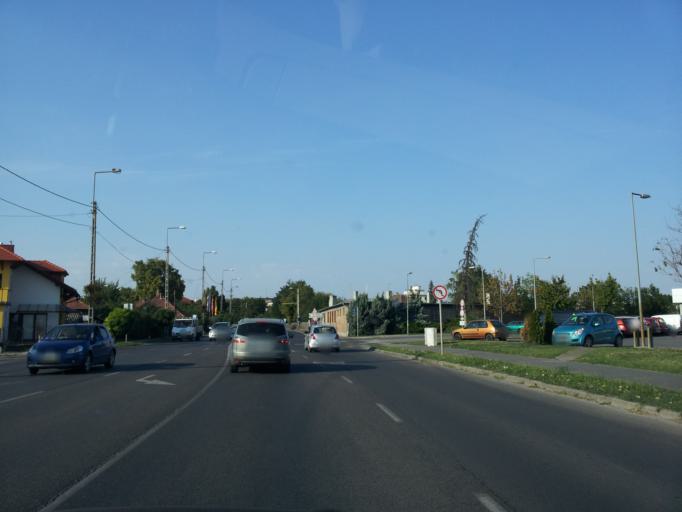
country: HU
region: Pest
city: Szentendre
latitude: 47.6514
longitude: 19.0709
